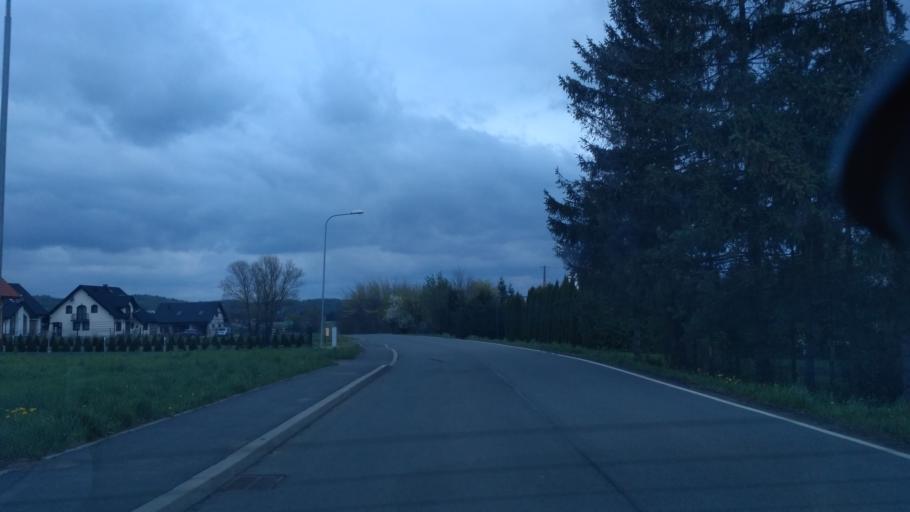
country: PL
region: Subcarpathian Voivodeship
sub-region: Powiat brzozowski
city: Jasionow
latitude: 49.6528
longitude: 21.9830
